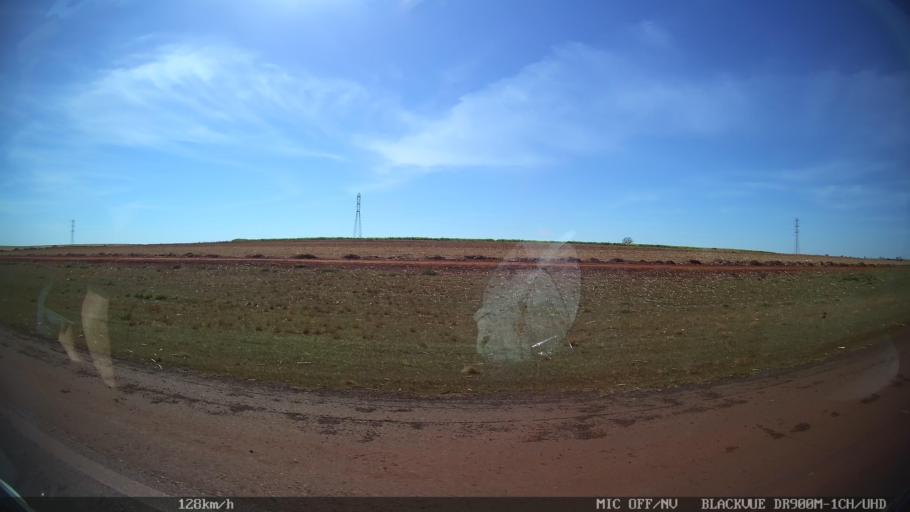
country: BR
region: Sao Paulo
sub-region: Ipua
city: Ipua
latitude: -20.4567
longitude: -48.1563
